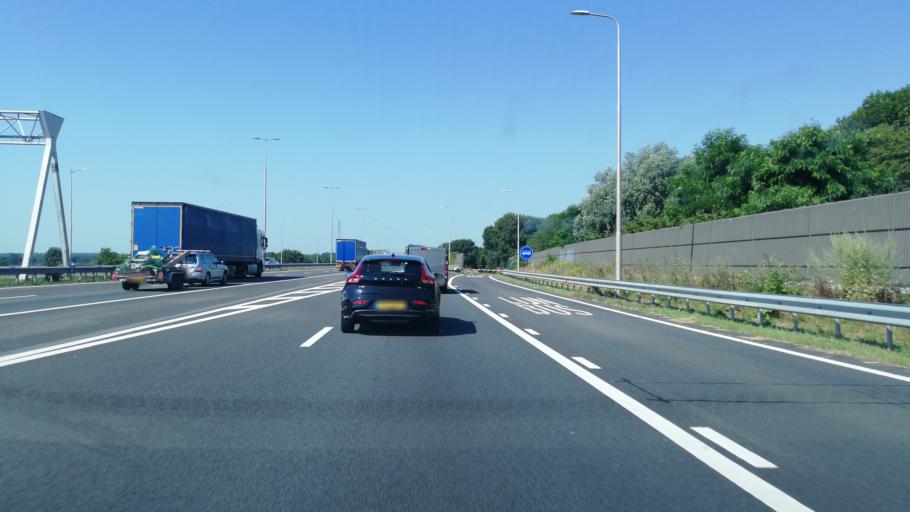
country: NL
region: Gelderland
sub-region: Gemeente Apeldoorn
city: Apeldoorn
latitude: 52.1847
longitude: 6.0103
